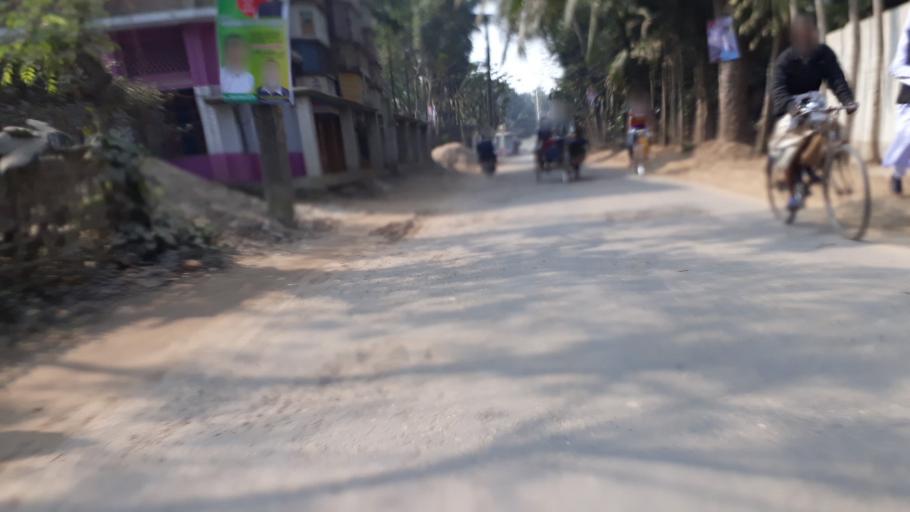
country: BD
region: Khulna
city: Kaliganj
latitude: 23.3535
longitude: 88.9082
